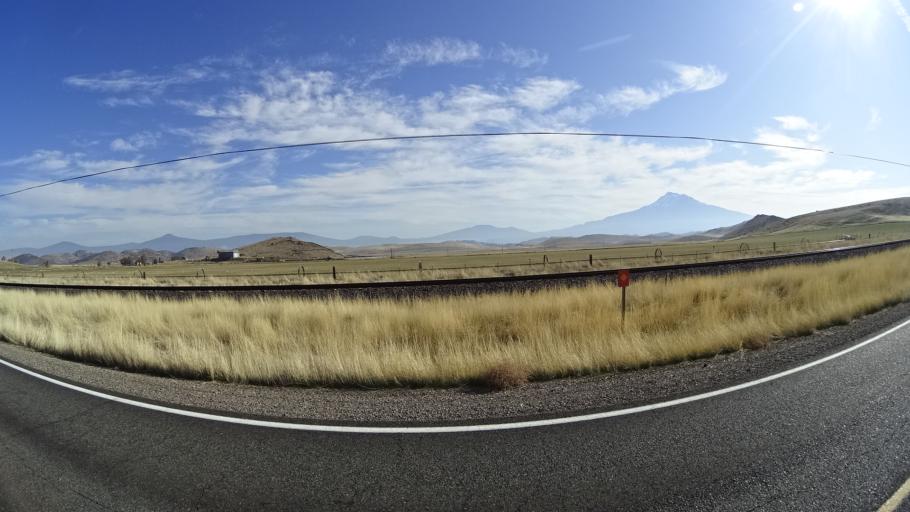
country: US
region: California
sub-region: Siskiyou County
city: Montague
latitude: 41.5588
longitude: -122.5267
